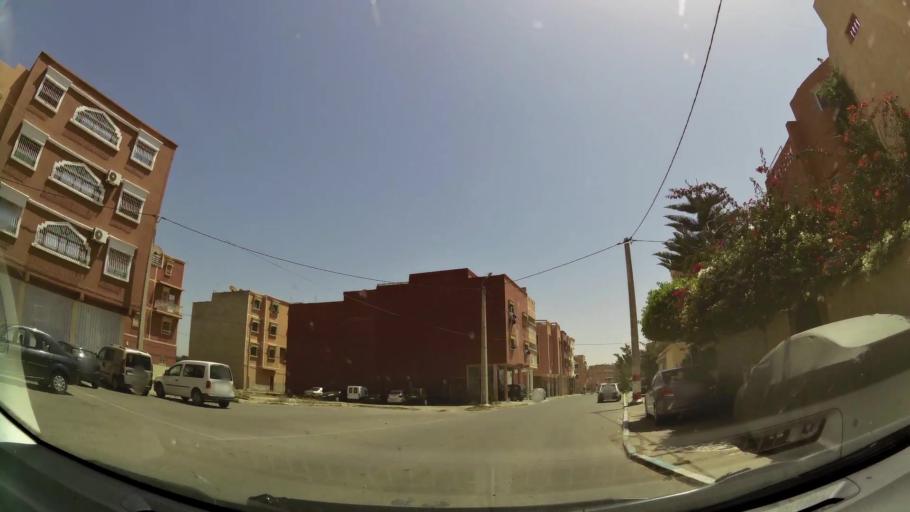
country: MA
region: Souss-Massa-Draa
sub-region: Inezgane-Ait Mellou
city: Inezgane
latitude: 30.3520
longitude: -9.4896
